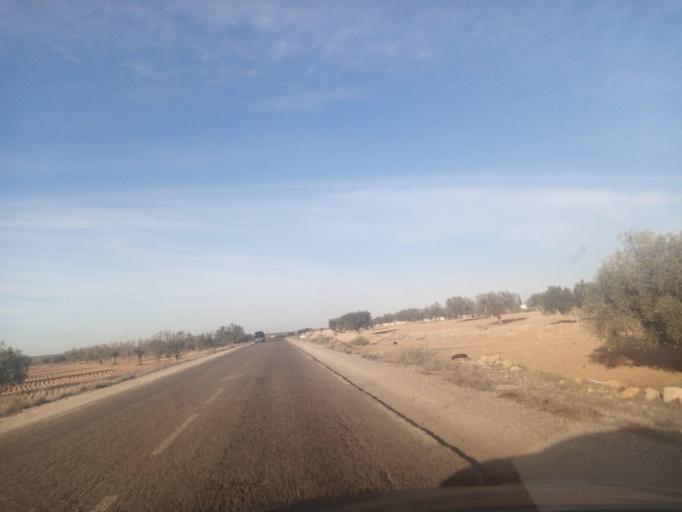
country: TN
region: Al Mahdiyah
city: Shurban
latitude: 34.9526
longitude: 10.3573
